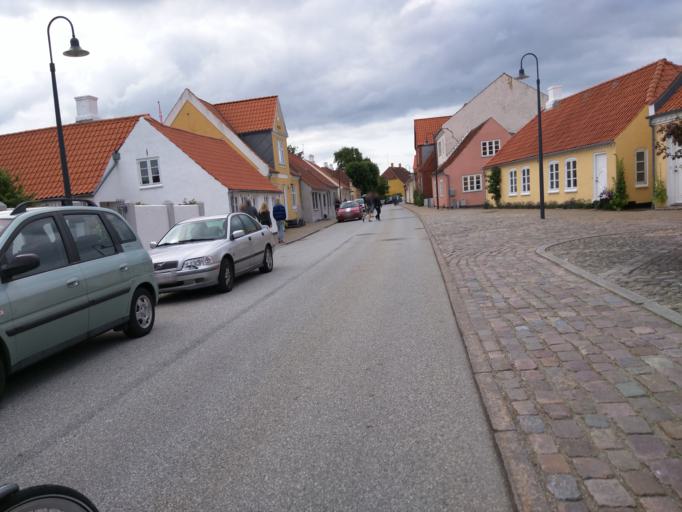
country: DK
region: North Denmark
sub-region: Frederikshavn Kommune
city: Saeby
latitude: 57.3334
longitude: 10.5269
